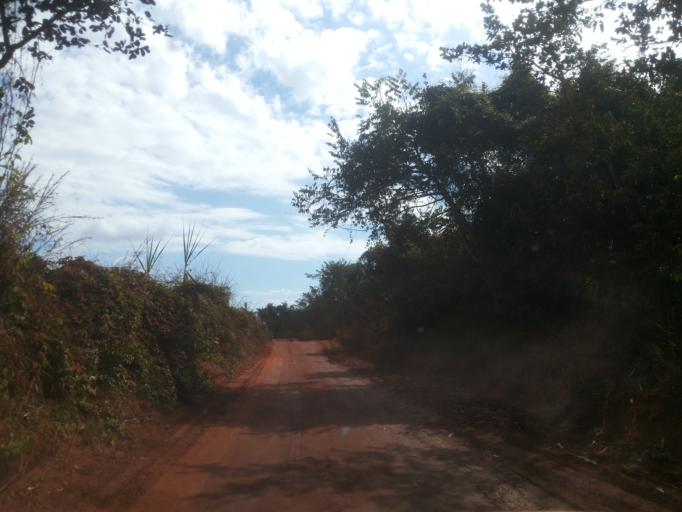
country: BR
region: Minas Gerais
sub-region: Ituiutaba
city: Ituiutaba
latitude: -19.0117
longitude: -49.3986
